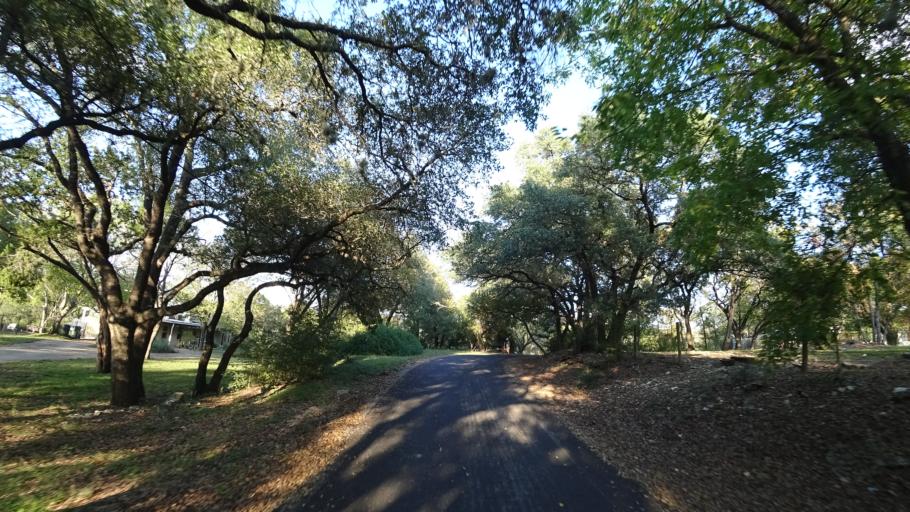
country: US
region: Texas
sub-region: Travis County
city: Lost Creek
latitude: 30.2966
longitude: -97.8457
